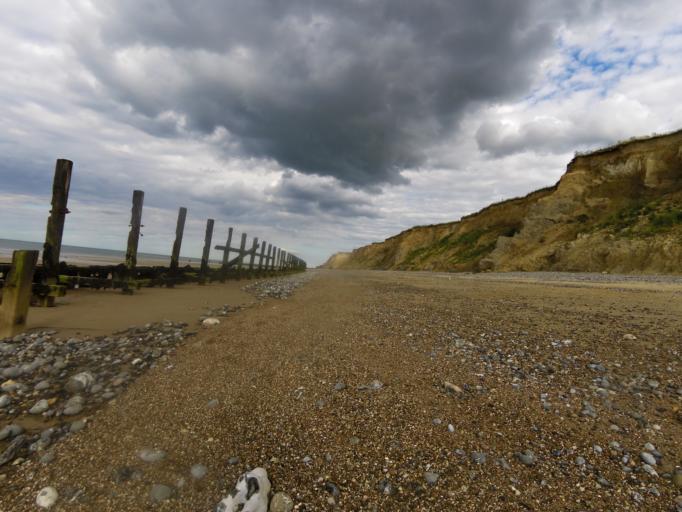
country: GB
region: England
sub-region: Norfolk
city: Sheringham
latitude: 52.9431
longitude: 1.2336
